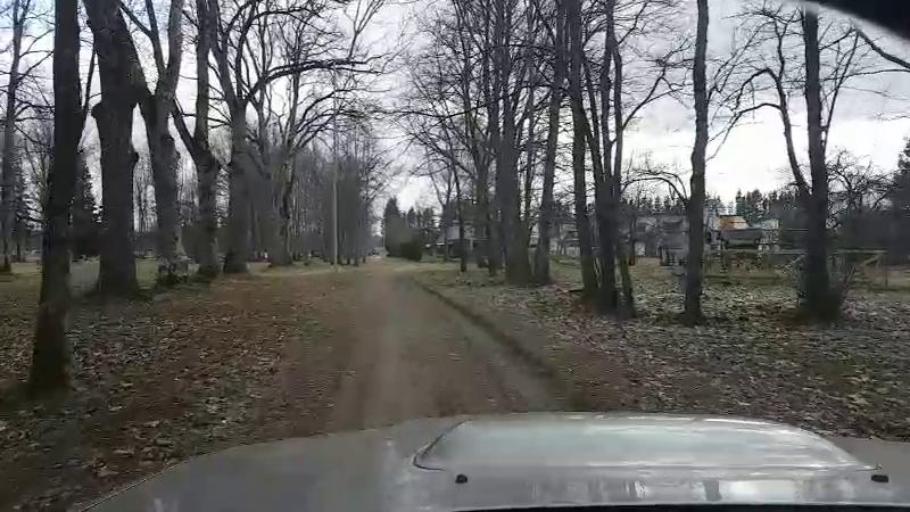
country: EE
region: Jaervamaa
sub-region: Paide linn
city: Paide
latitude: 58.8815
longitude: 25.5409
